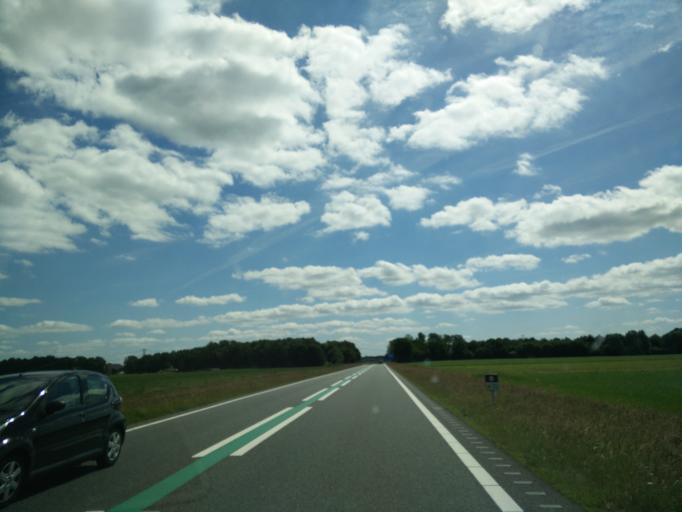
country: NL
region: Drenthe
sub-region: Gemeente Coevorden
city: Sleen
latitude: 52.7945
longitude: 6.8295
